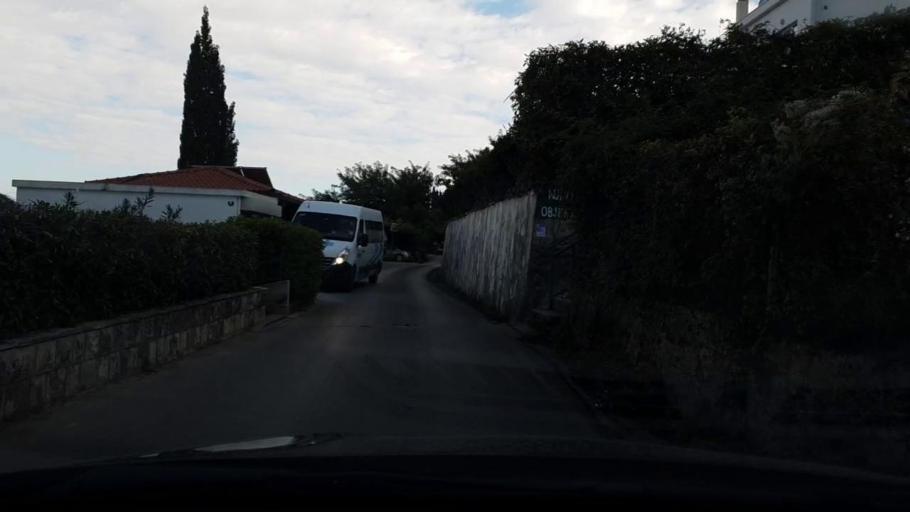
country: ME
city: Igalo
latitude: 42.4378
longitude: 18.5111
